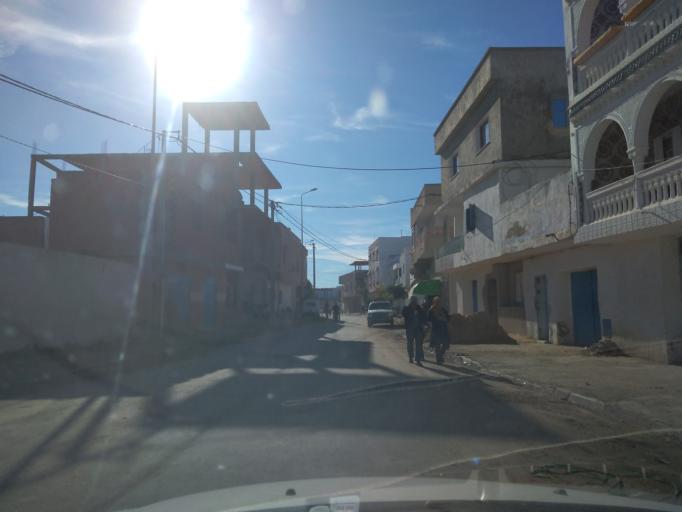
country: TN
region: Ariana
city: Qal'at al Andalus
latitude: 37.0672
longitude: 10.1218
